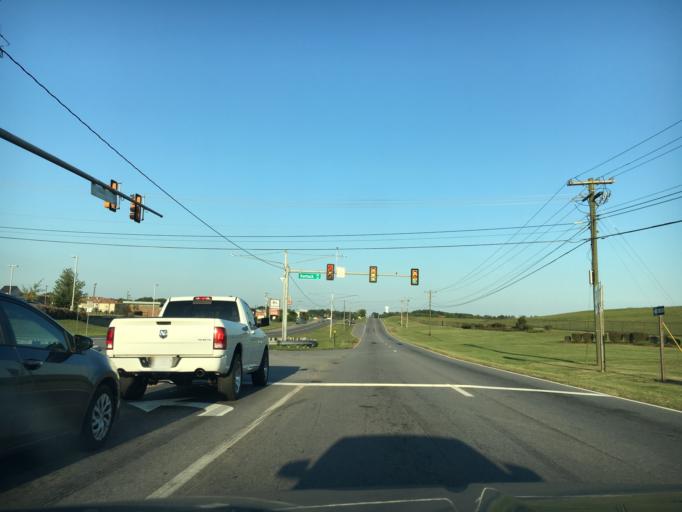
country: US
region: Virginia
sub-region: City of Danville
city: Danville
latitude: 36.5809
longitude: -79.3405
